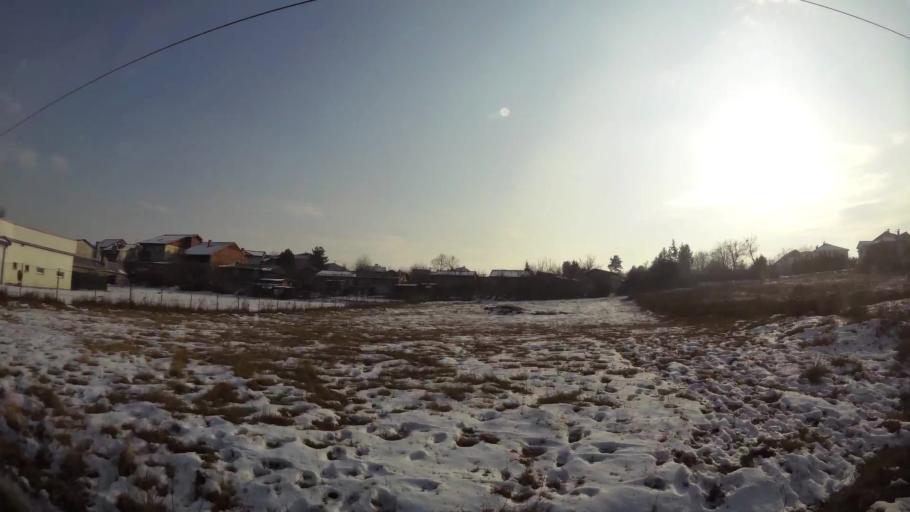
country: MK
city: Creshevo
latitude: 42.0183
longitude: 21.5056
